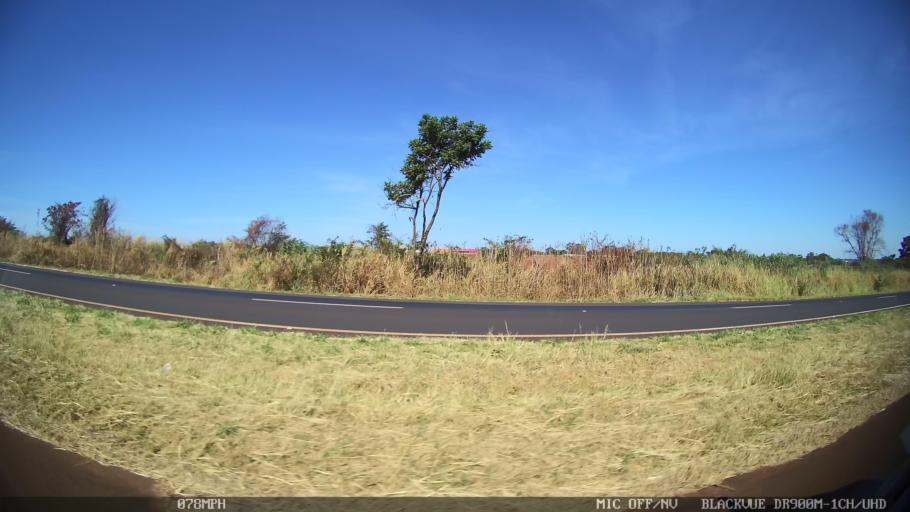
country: BR
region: Sao Paulo
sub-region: Barretos
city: Barretos
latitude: -20.5185
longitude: -48.5740
